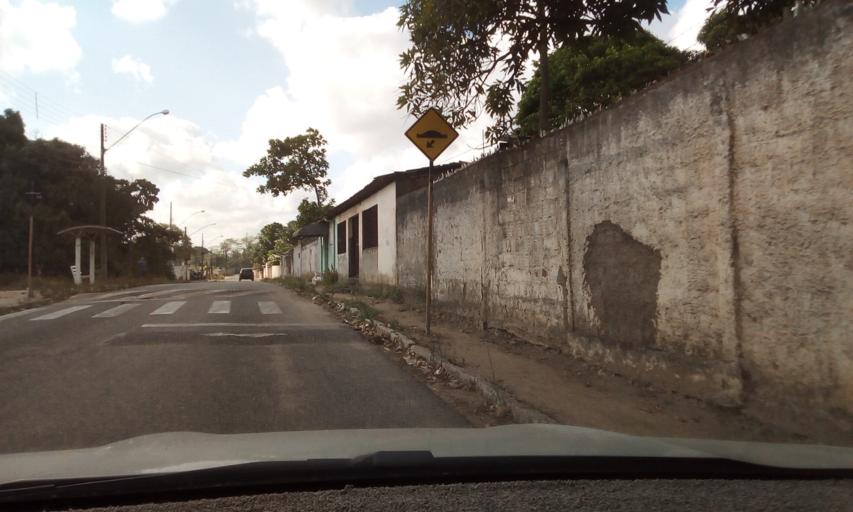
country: BR
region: Paraiba
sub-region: Bayeux
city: Bayeux
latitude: -7.1485
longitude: -34.9054
